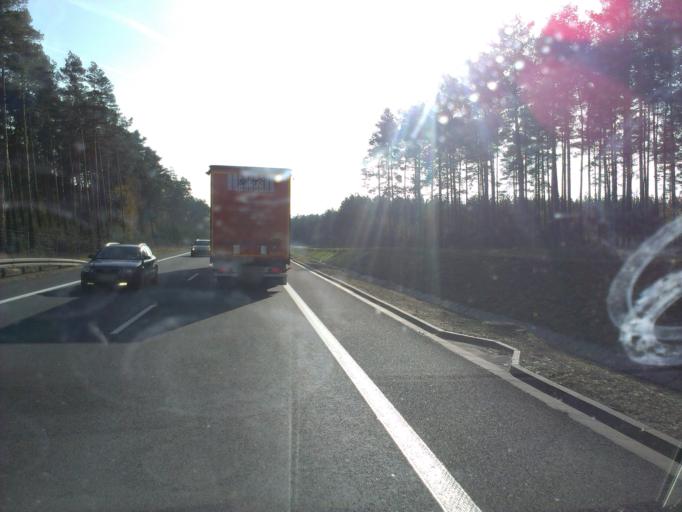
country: PL
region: Lubusz
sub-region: Powiat nowosolski
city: Nowa Sol
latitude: 51.8122
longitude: 15.6758
